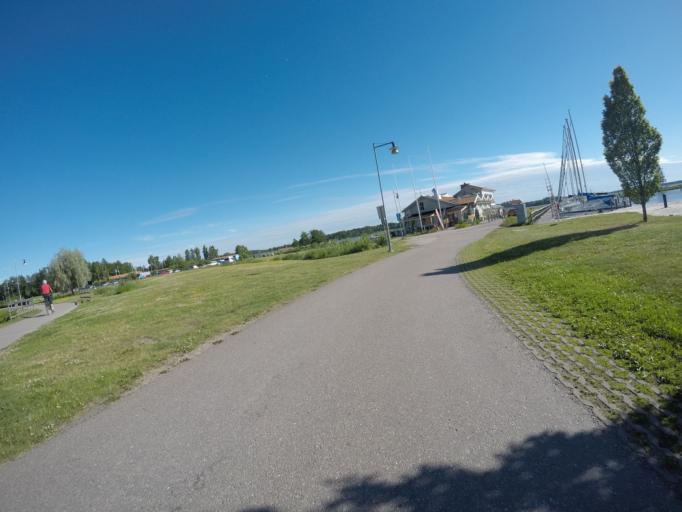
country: SE
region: Vaestmanland
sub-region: Vasteras
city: Vasteras
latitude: 59.5969
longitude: 16.5867
